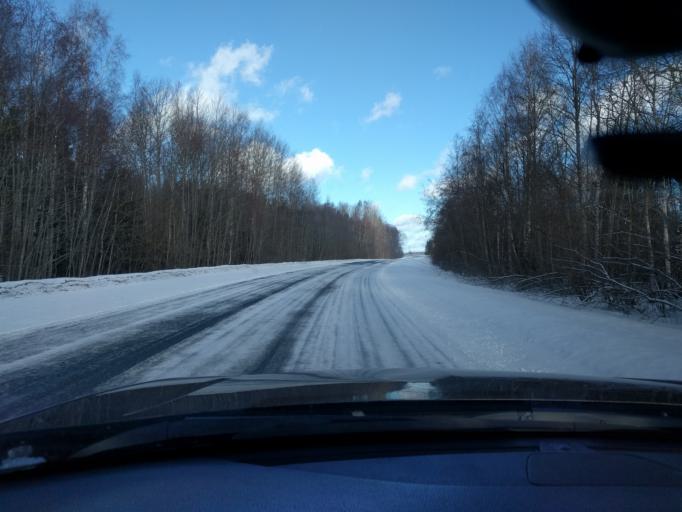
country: EE
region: Harju
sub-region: Raasiku vald
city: Raasiku
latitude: 59.3208
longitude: 25.1583
